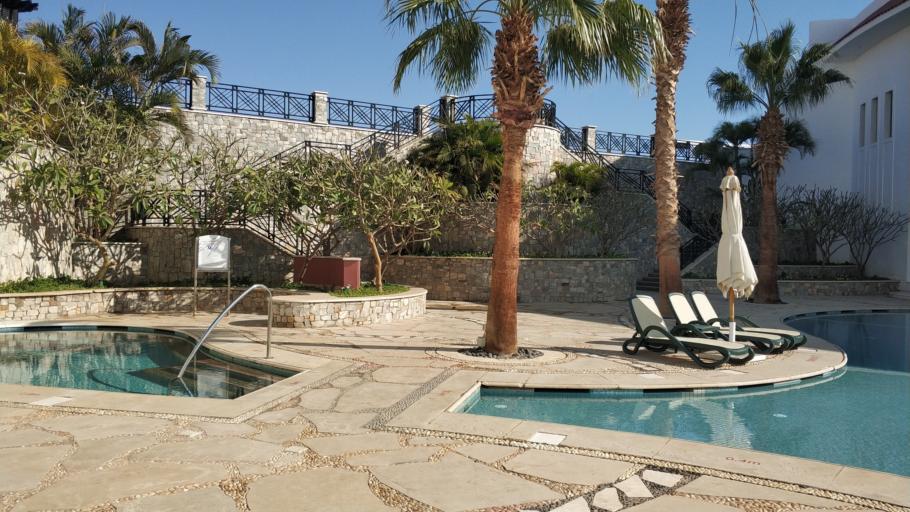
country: EG
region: South Sinai
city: Sharm el-Sheikh
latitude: 27.9162
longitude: 34.3609
